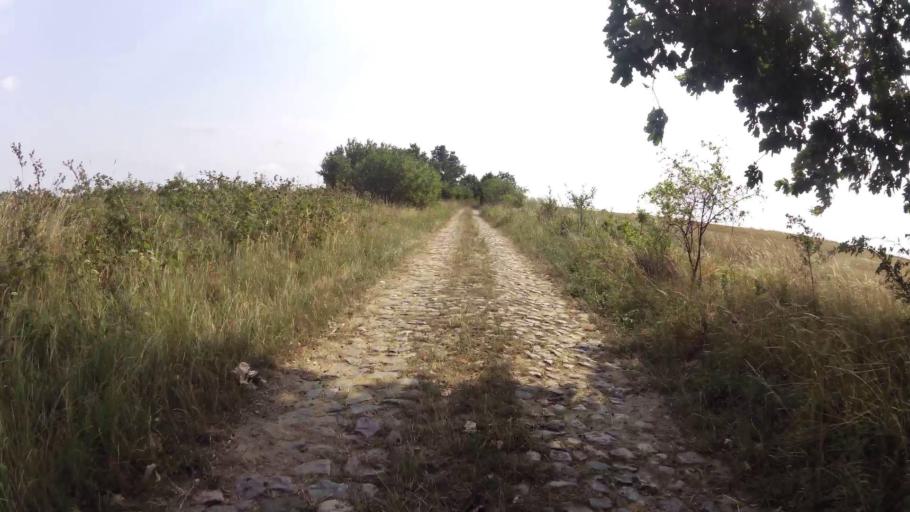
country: PL
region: West Pomeranian Voivodeship
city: Trzcinsko Zdroj
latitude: 52.8966
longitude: 14.5226
